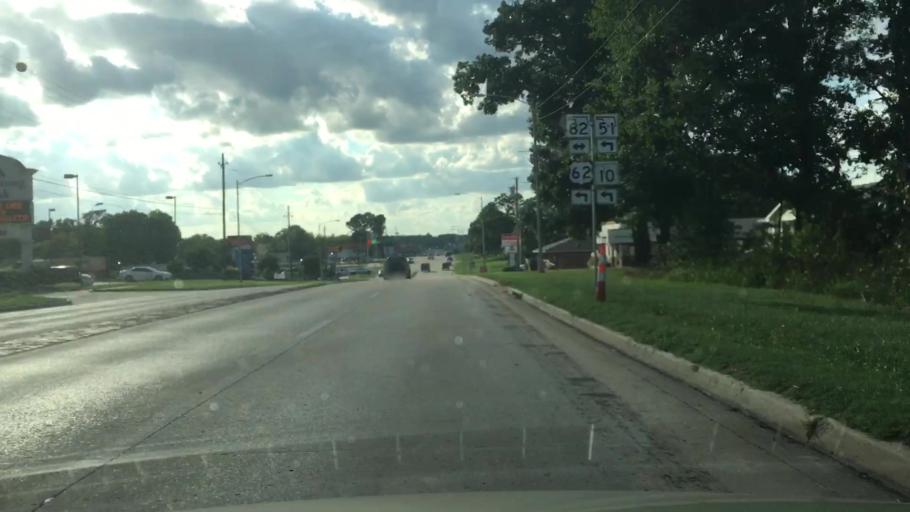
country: US
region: Oklahoma
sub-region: Cherokee County
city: Tahlequah
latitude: 35.9154
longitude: -94.9508
